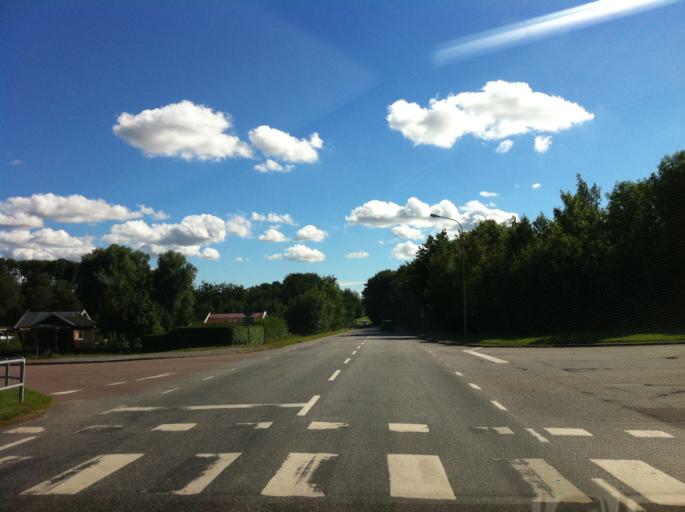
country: SE
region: Skane
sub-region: Svalovs Kommun
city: Kagerod
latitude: 56.0245
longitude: 13.1105
